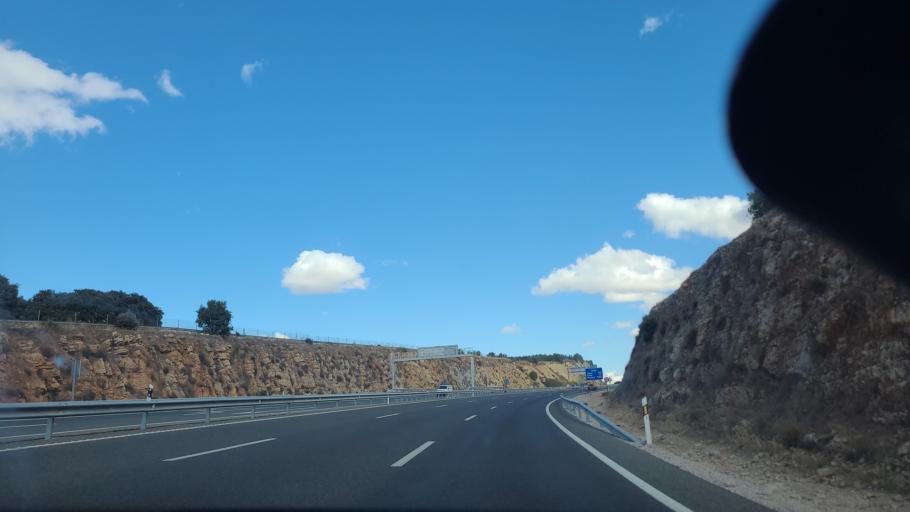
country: ES
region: Andalusia
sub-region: Provincia de Granada
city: Iznalloz
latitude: 37.4137
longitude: -3.5627
